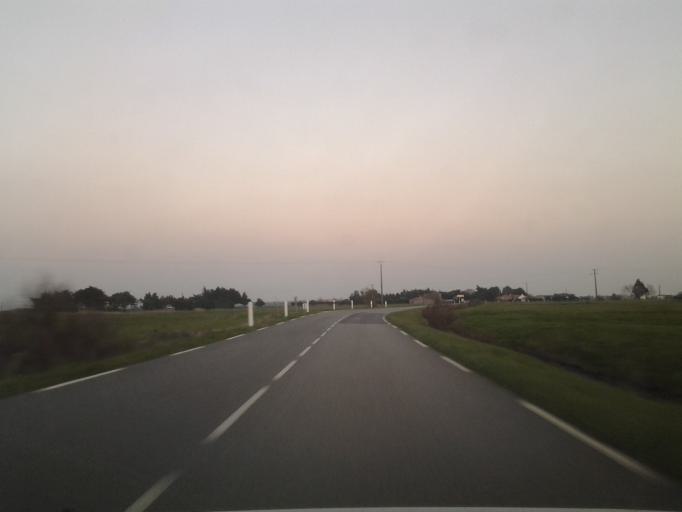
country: FR
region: Pays de la Loire
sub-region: Departement de la Vendee
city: Beauvoir-sur-Mer
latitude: 46.9208
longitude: -2.0867
